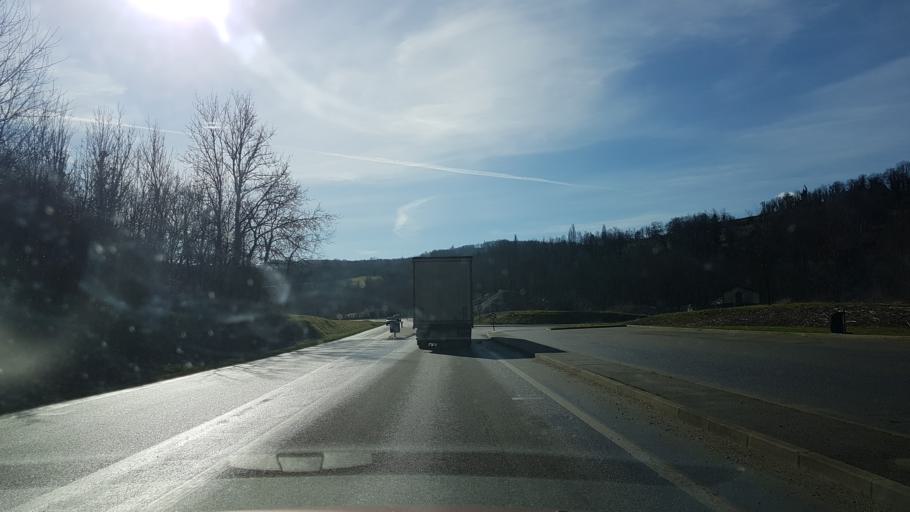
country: FR
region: Rhone-Alpes
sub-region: Departement de la Haute-Savoie
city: Frangy
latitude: 46.0227
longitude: 5.9106
